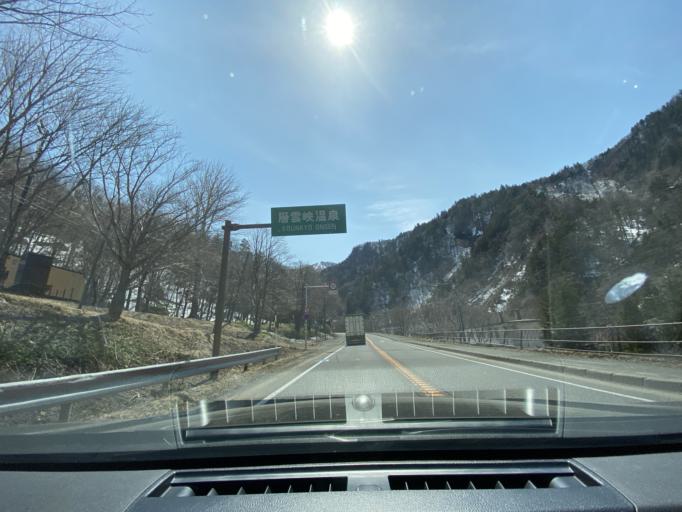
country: JP
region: Hokkaido
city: Kamikawa
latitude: 43.7331
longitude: 142.9425
